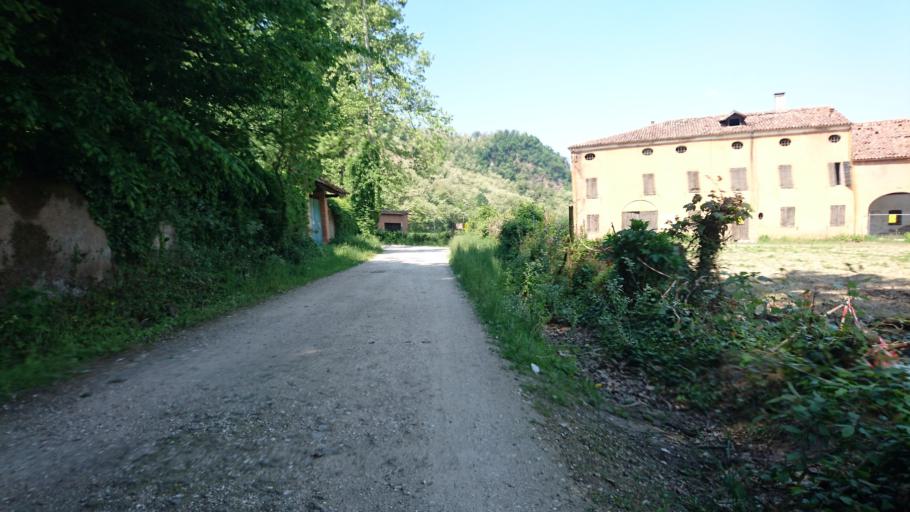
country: IT
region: Veneto
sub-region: Provincia di Padova
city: San Biagio
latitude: 45.3684
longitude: 11.7591
